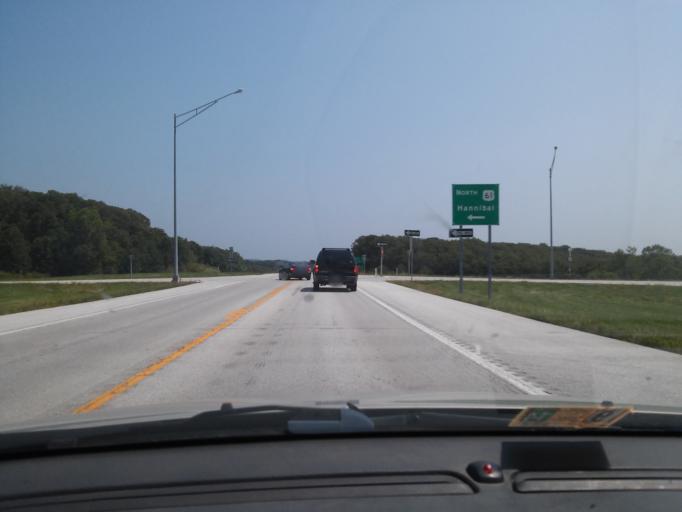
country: US
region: Missouri
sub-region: Pike County
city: Bowling Green
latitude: 39.3608
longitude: -91.2014
